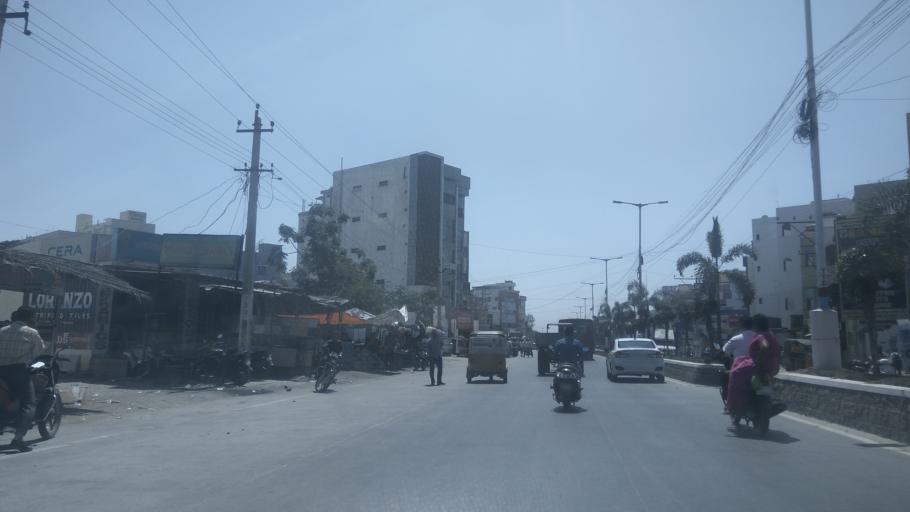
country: IN
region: Andhra Pradesh
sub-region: Chittoor
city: Tirupati
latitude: 13.6158
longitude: 79.4356
